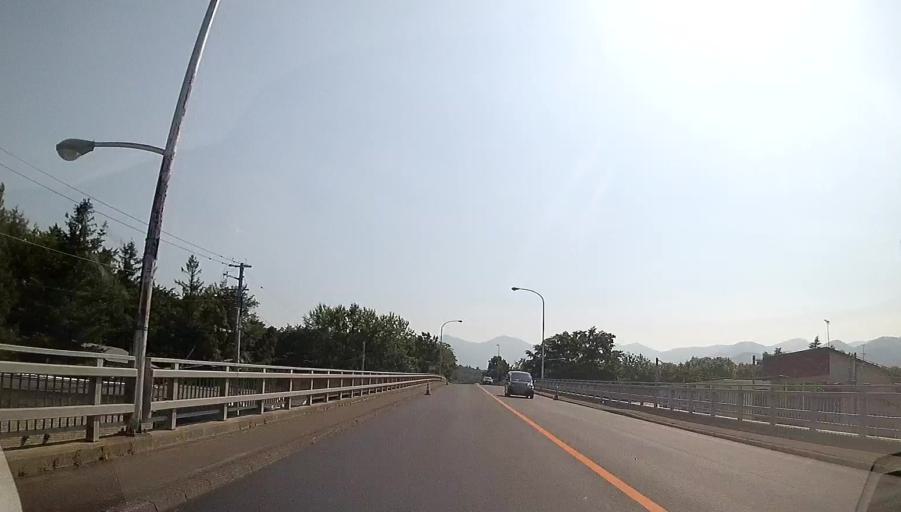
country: JP
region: Hokkaido
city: Otofuke
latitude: 43.0094
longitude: 142.8823
